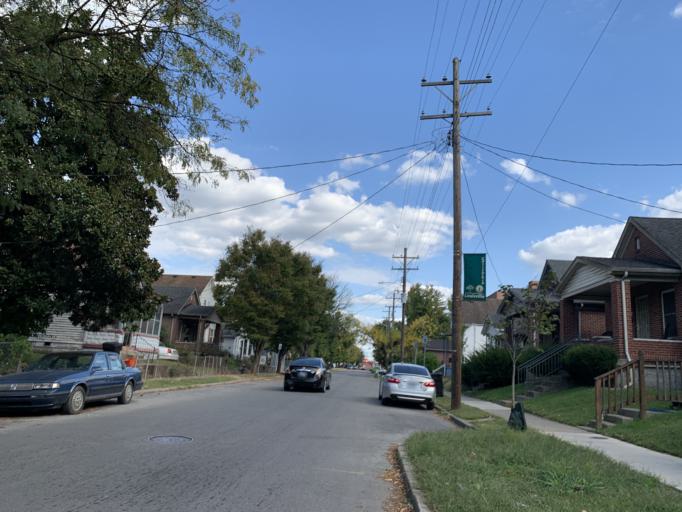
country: US
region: Kentucky
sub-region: Jefferson County
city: Louisville
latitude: 38.2432
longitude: -85.7831
